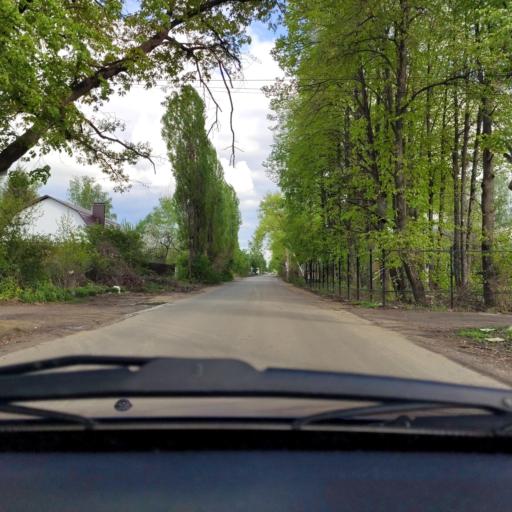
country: RU
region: Voronezj
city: Voronezh
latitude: 51.6020
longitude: 39.1618
